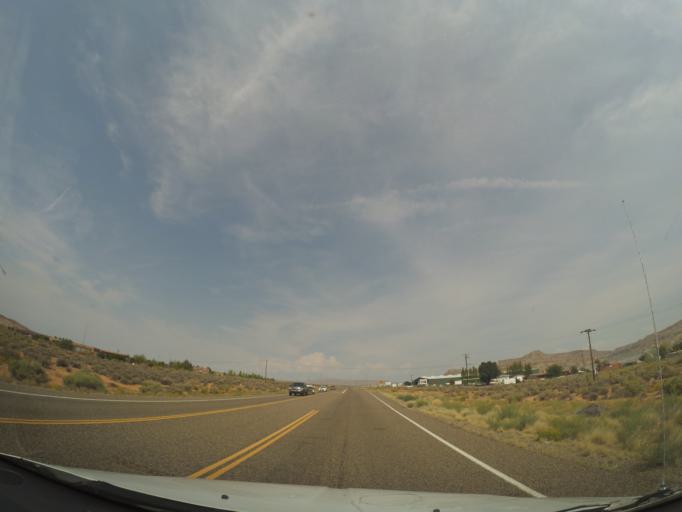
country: US
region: Arizona
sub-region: Coconino County
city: Page
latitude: 37.0621
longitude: -111.6434
